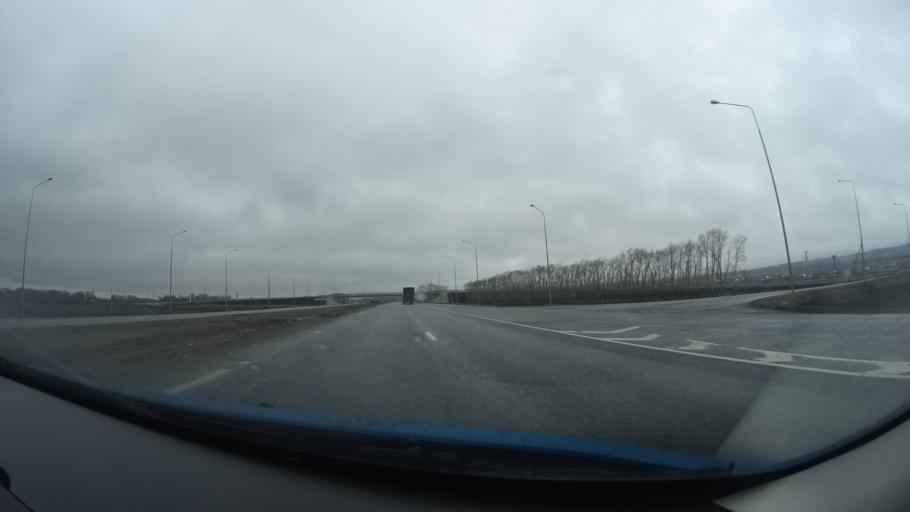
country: RU
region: Bashkortostan
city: Alekseyevka
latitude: 54.7248
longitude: 54.9263
